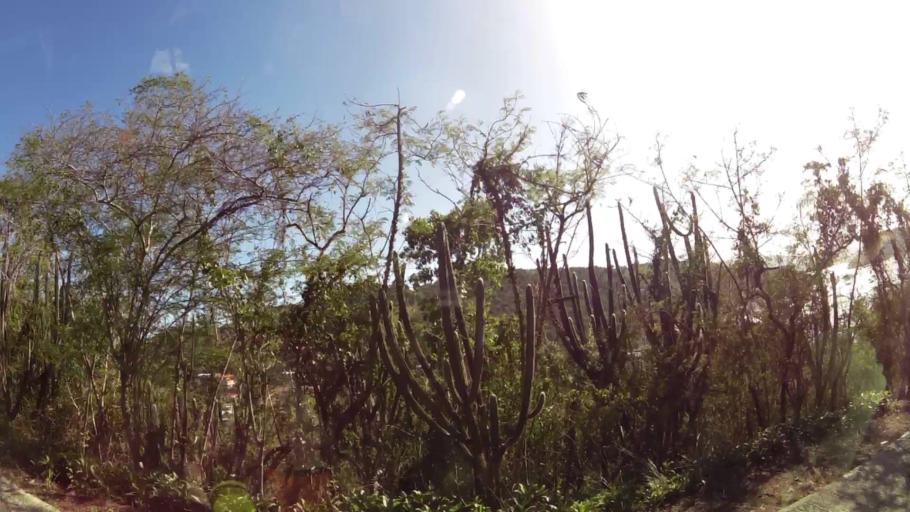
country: VG
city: Road Town
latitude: 18.3885
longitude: -64.6989
